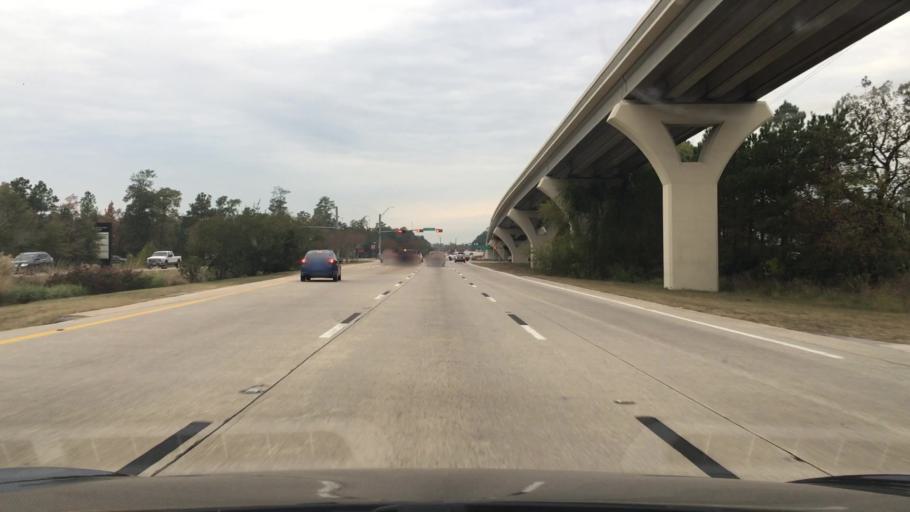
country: US
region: Texas
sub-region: Montgomery County
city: Shenandoah
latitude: 30.2074
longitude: -95.4591
